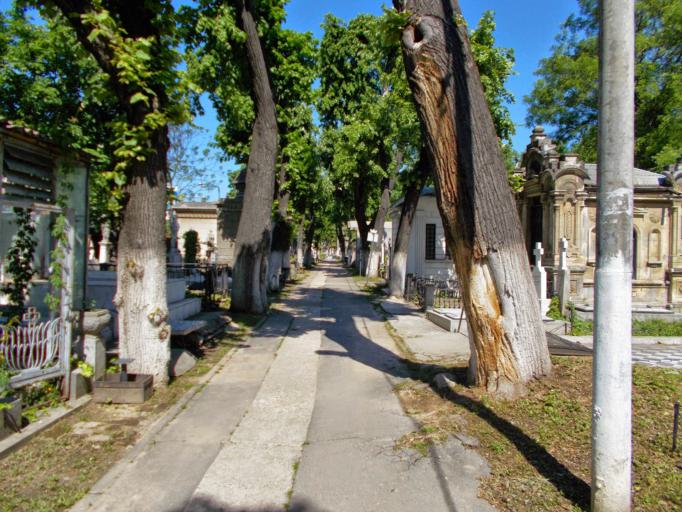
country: RO
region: Bucuresti
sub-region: Municipiul Bucuresti
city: Bucuresti
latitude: 44.4036
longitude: 26.0979
